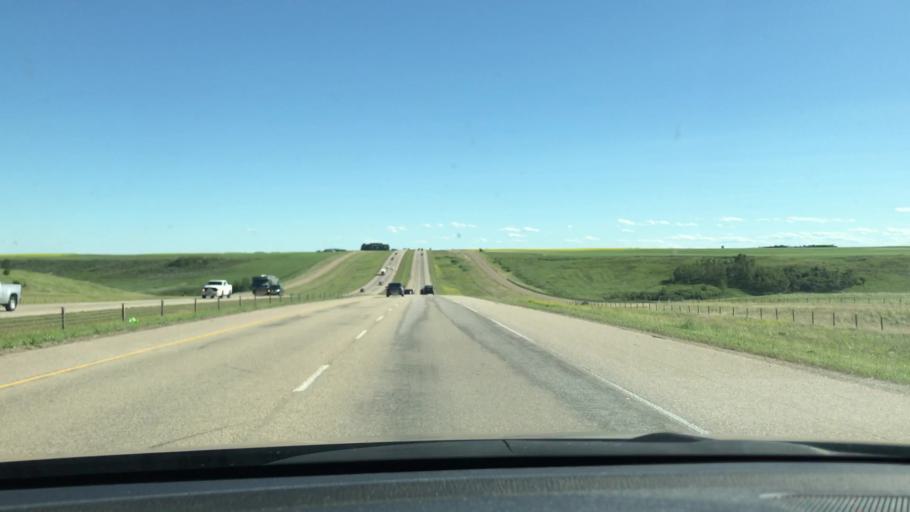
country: CA
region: Alberta
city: Carstairs
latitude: 51.6024
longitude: -114.0255
